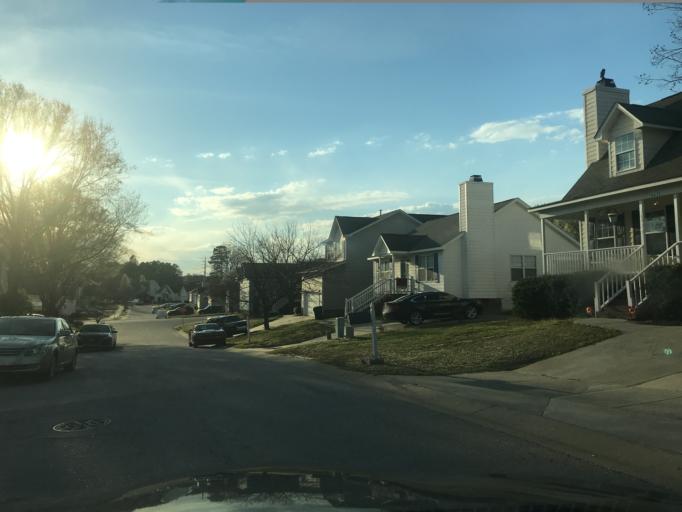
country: US
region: North Carolina
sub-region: Wake County
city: Raleigh
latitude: 35.8555
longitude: -78.5678
